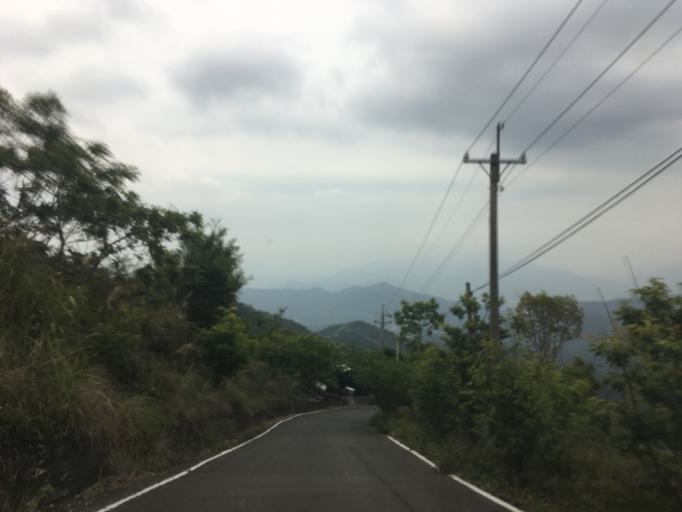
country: TW
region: Taiwan
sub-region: Nantou
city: Puli
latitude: 23.9623
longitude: 120.8456
